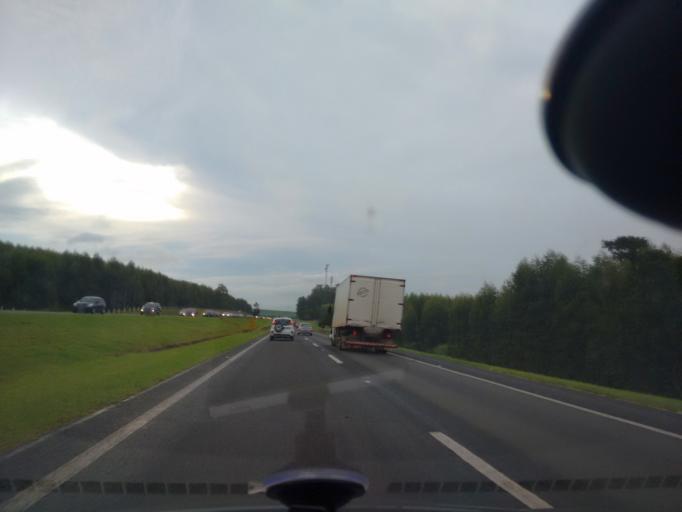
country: BR
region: Sao Paulo
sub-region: Itirapina
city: Itirapina
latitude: -22.2290
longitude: -47.7444
